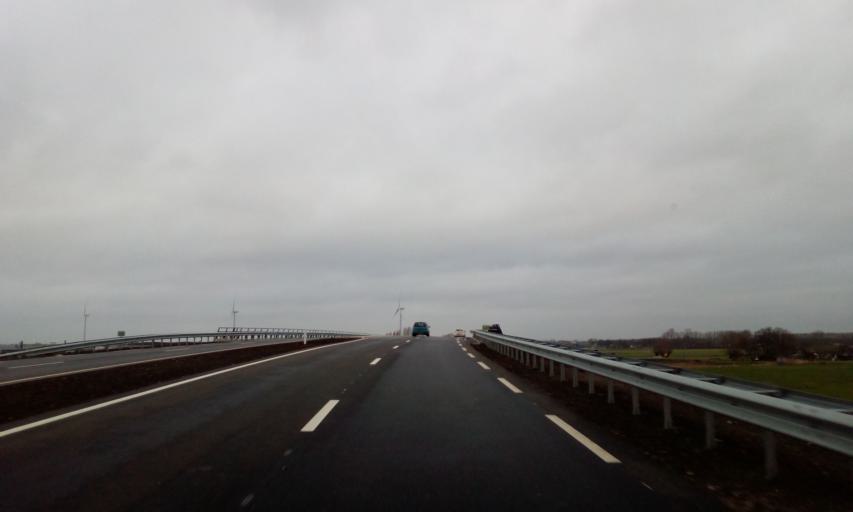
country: NL
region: South Holland
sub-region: Gemeente Waddinxveen
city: Waddinxveen
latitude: 52.0083
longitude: 4.6463
